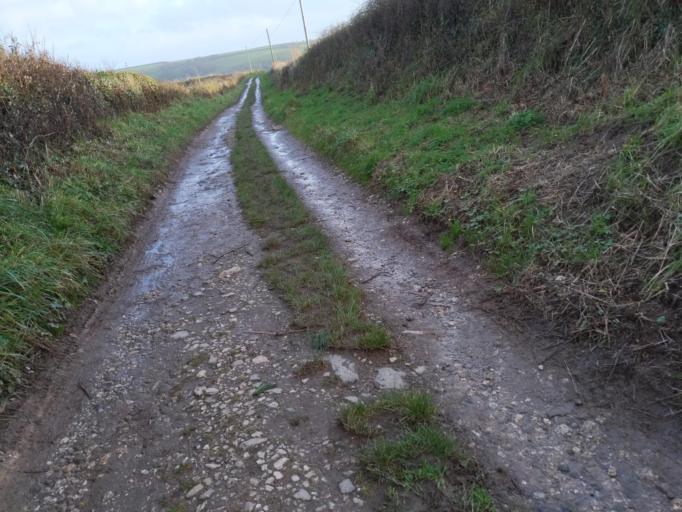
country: GB
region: England
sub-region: Devon
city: Wembury
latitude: 50.3176
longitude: -4.0618
